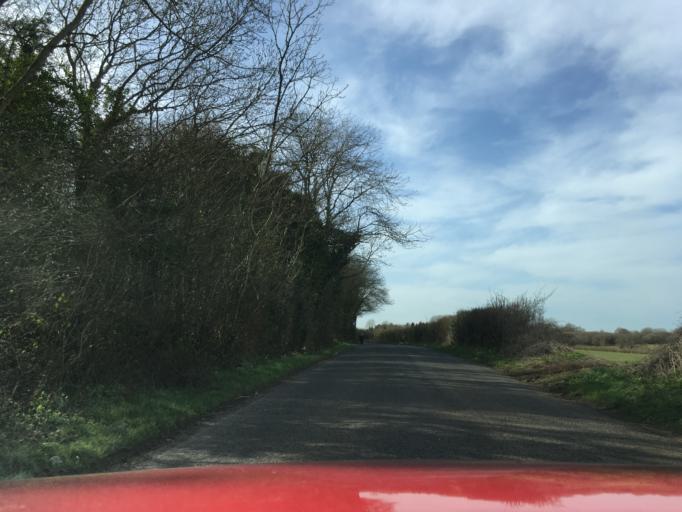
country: GB
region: England
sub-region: Wiltshire
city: Norton
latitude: 51.5205
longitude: -2.1491
